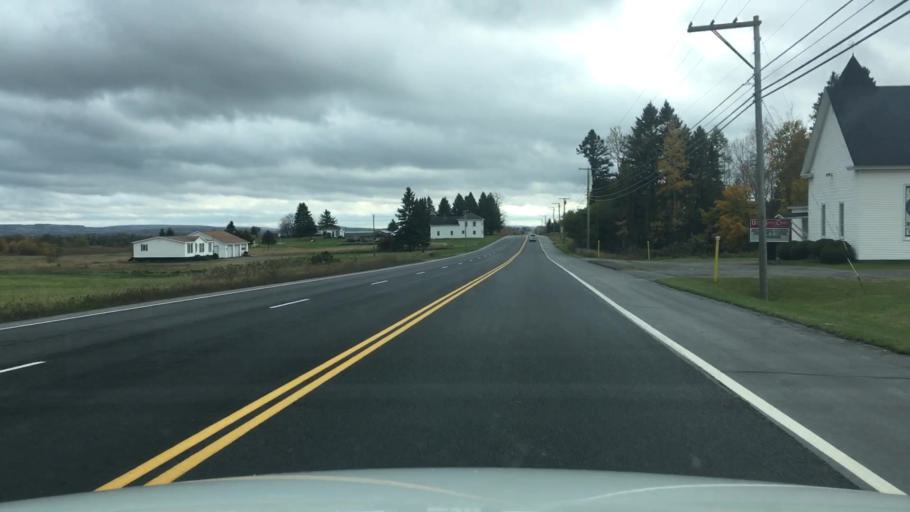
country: US
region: Maine
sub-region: Aroostook County
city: Houlton
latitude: 46.2249
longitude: -67.8410
